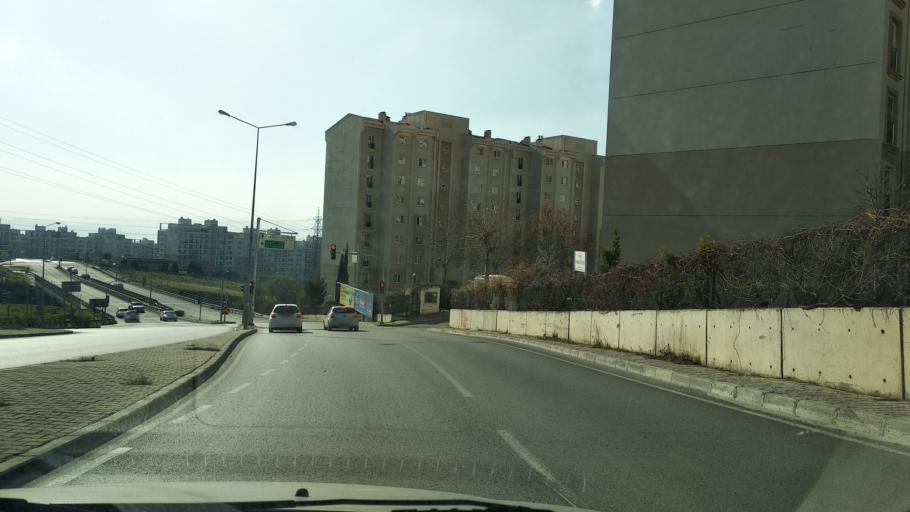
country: TR
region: Izmir
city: Karsiyaka
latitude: 38.4914
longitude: 27.0911
